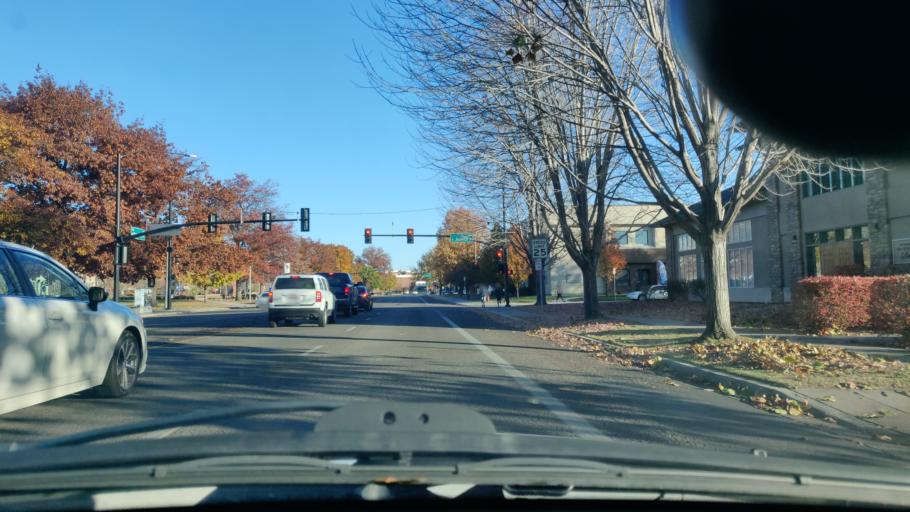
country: US
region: Idaho
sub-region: Ada County
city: Boise
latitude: 43.6036
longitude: -116.2067
